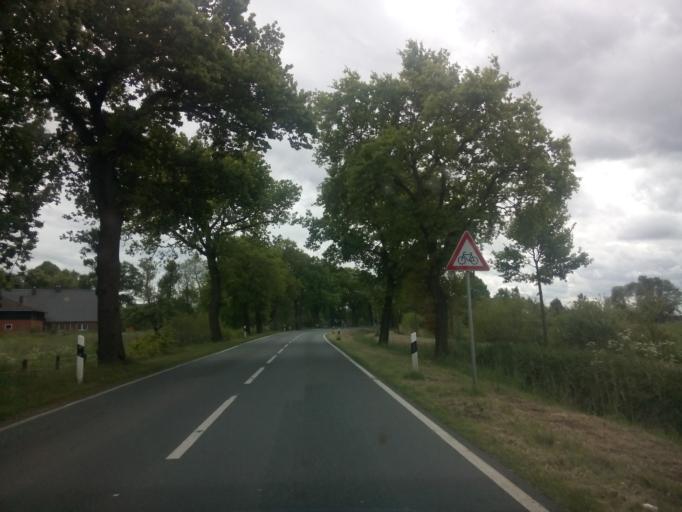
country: DE
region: Lower Saxony
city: Delmenhorst
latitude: 53.1069
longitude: 8.6461
